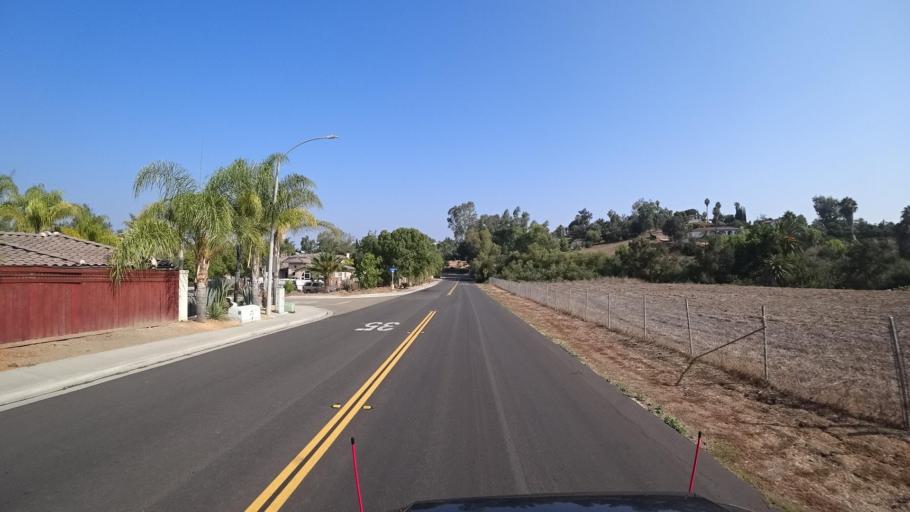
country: US
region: California
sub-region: San Diego County
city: Vista
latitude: 33.2329
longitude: -117.2437
